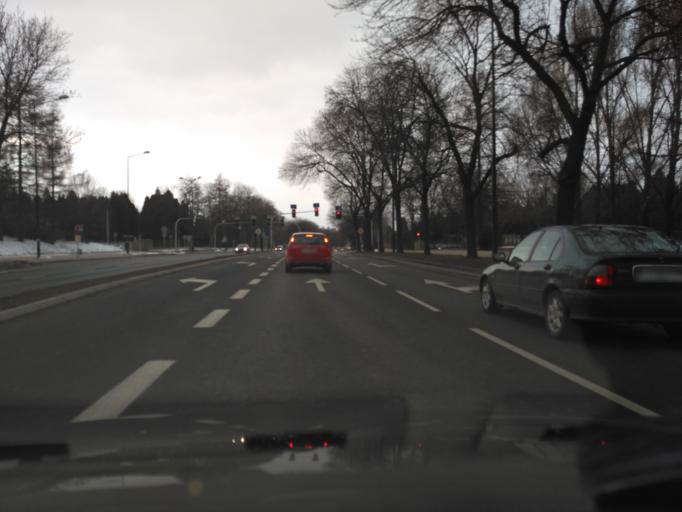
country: PL
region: Lublin Voivodeship
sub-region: Powiat lubelski
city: Lublin
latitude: 51.2593
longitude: 22.5807
